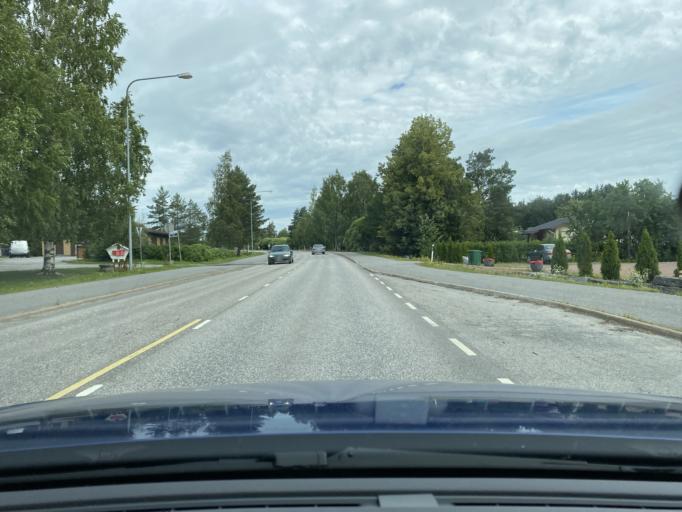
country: FI
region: Ostrobothnia
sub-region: Vaasa
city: Vaehaekyroe
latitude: 63.0481
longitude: 22.1160
